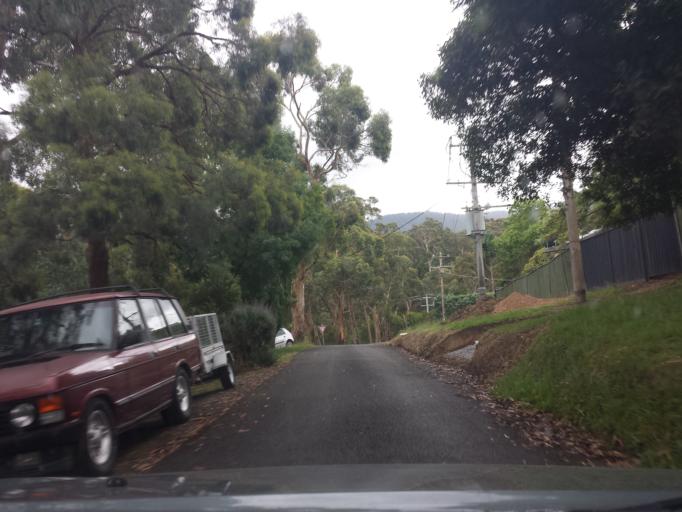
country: AU
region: Victoria
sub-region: Yarra Ranges
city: Belgrave Heights
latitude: -37.9150
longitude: 145.3429
